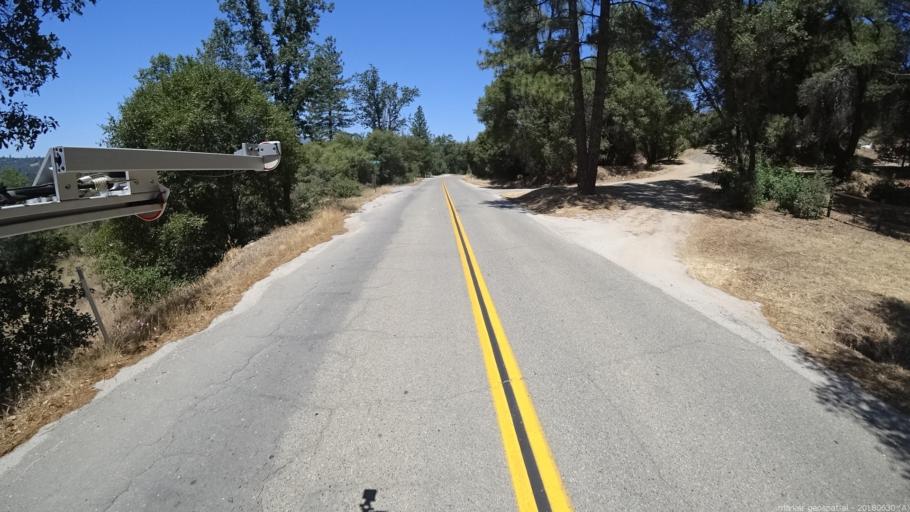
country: US
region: California
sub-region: Fresno County
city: Auberry
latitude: 37.2205
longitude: -119.4874
